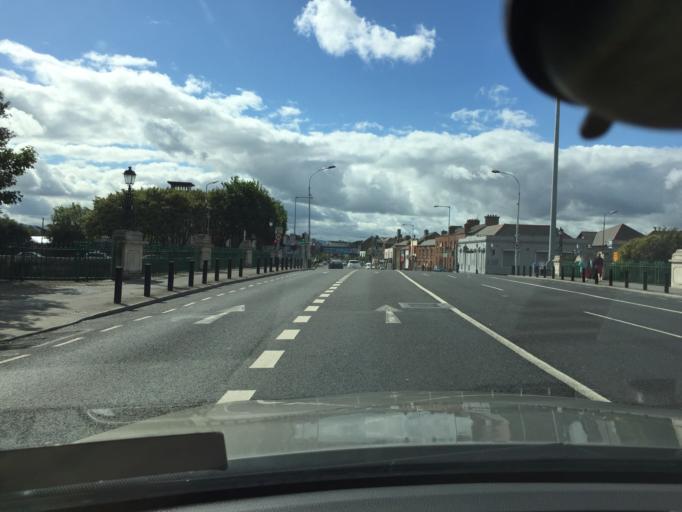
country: IE
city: Fairview
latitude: 53.3611
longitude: -6.2383
